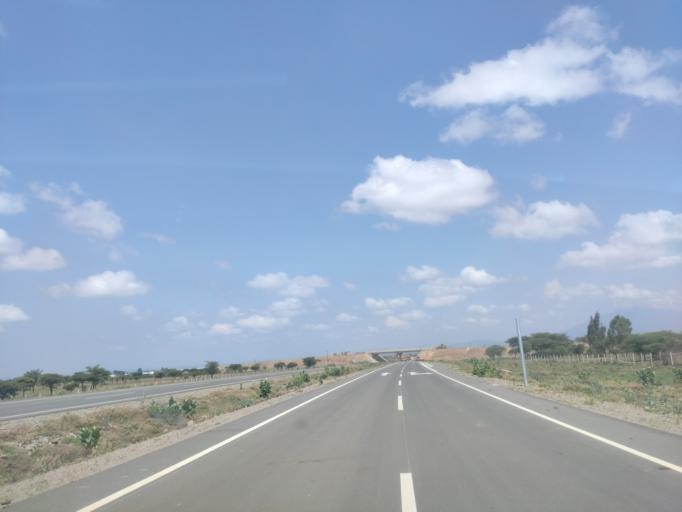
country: ET
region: Oromiya
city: Mojo
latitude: 8.5087
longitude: 39.0789
